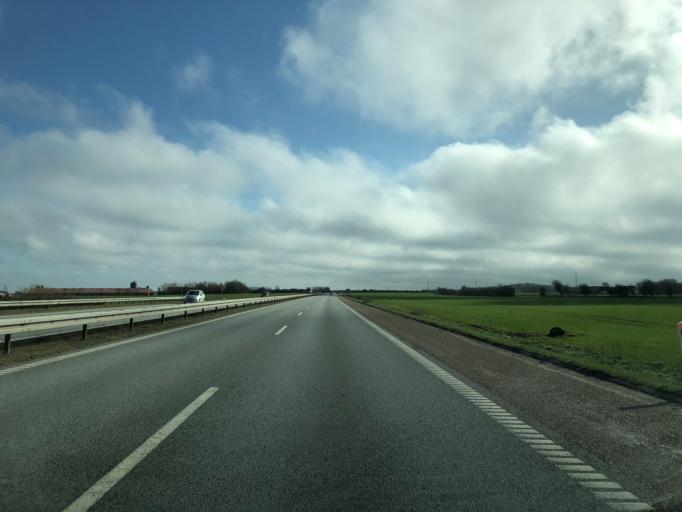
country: DK
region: North Denmark
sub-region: Hjorring Kommune
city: Hjorring
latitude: 57.4432
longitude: 10.0401
